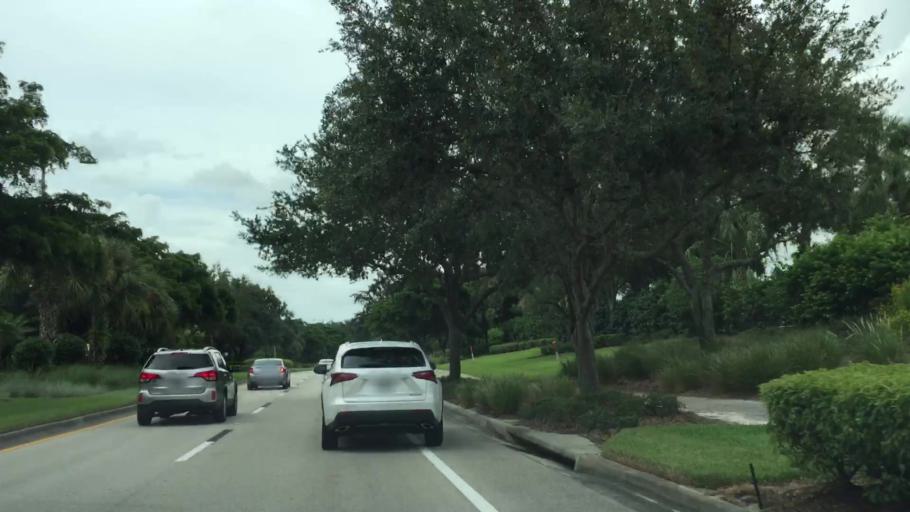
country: US
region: Florida
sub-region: Lee County
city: Estero
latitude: 26.3988
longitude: -81.7844
